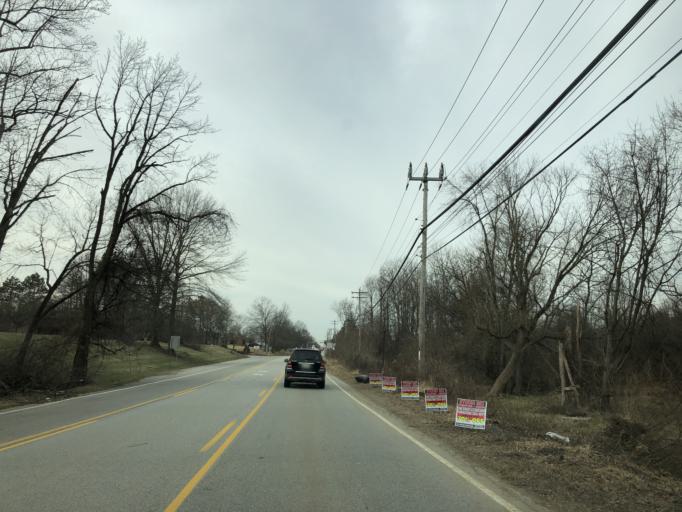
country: US
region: Pennsylvania
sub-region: Chester County
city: Exton
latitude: 40.0305
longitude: -75.6040
